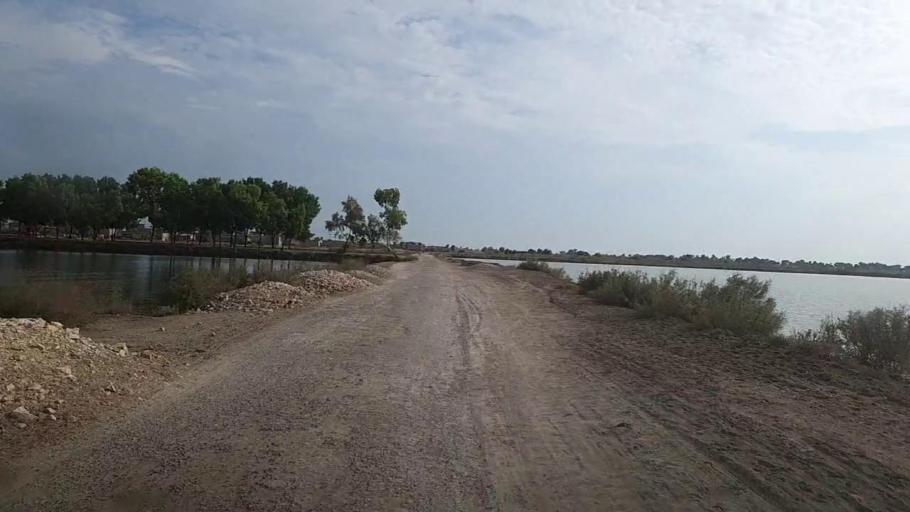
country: PK
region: Sindh
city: Thul
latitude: 28.2720
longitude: 68.8540
